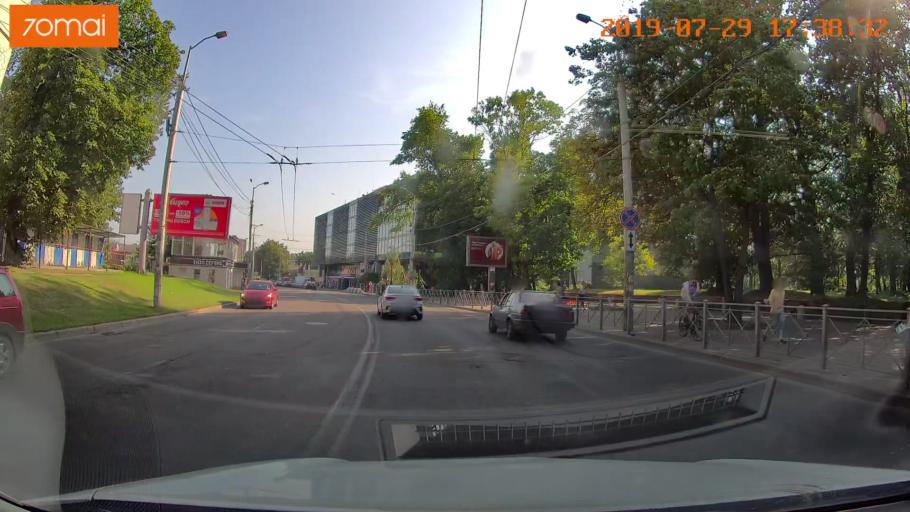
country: RU
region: Kaliningrad
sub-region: Gorod Kaliningrad
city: Kaliningrad
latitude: 54.7225
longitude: 20.5073
